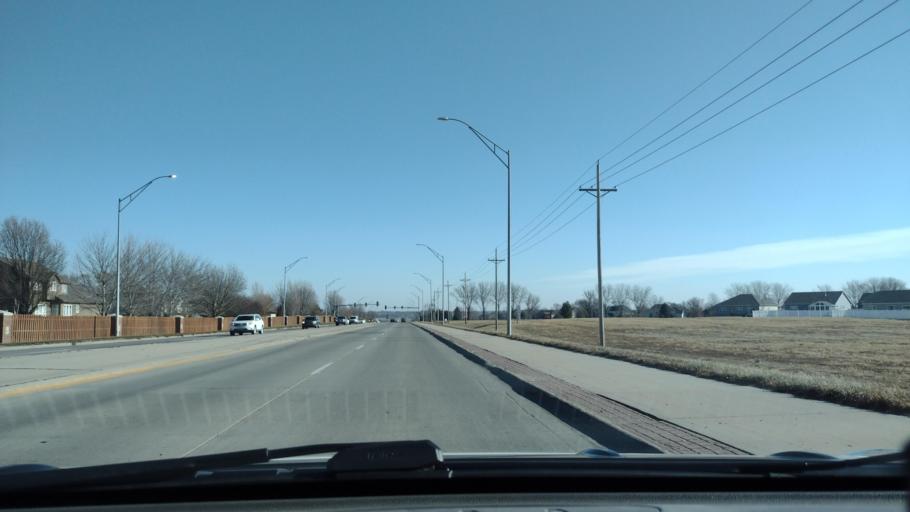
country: US
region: Nebraska
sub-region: Sarpy County
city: La Vista
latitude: 41.1617
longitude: -96.0077
